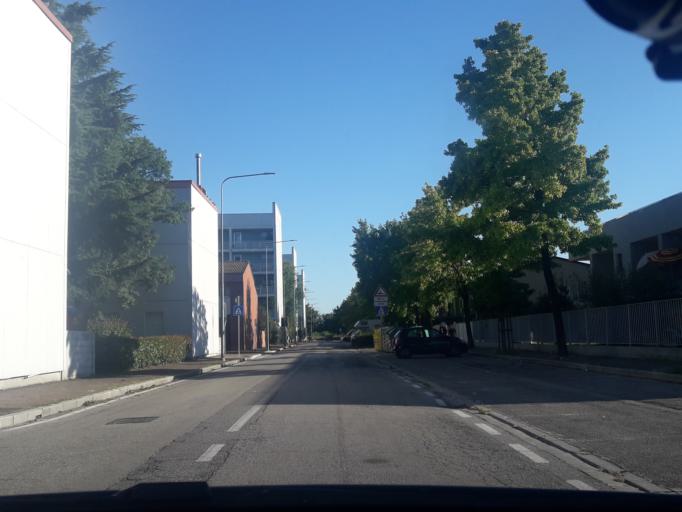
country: IT
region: Friuli Venezia Giulia
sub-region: Provincia di Udine
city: Passons
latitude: 46.0696
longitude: 13.2097
